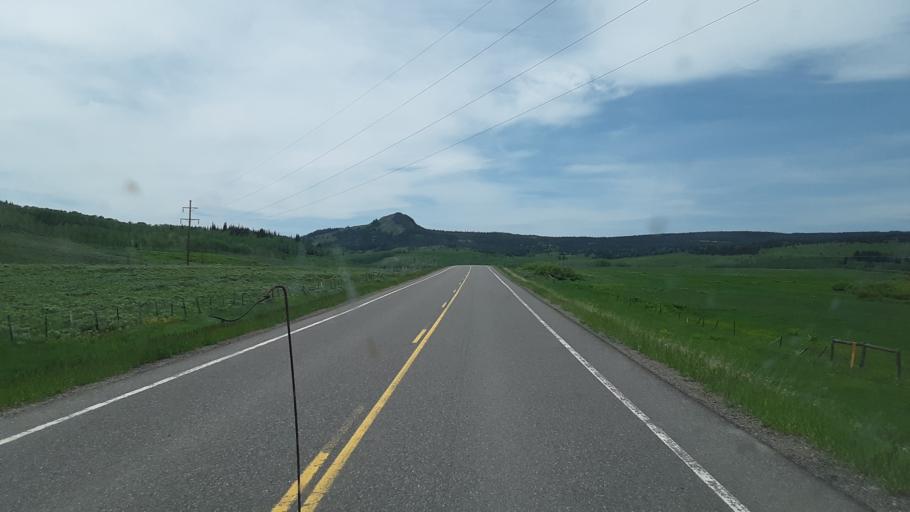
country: US
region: Colorado
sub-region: Routt County
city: Steamboat Springs
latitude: 40.3960
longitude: -106.5571
